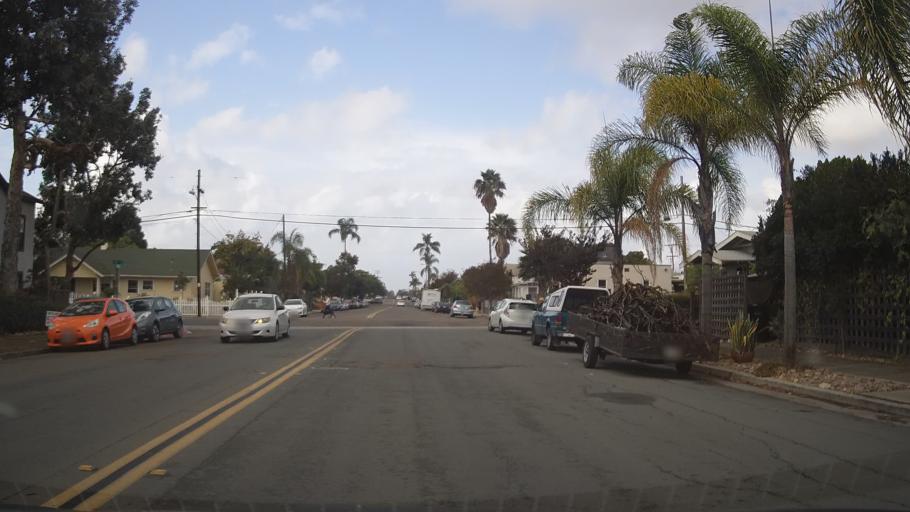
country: US
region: California
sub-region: San Diego County
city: San Diego
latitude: 32.7297
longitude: -117.1269
